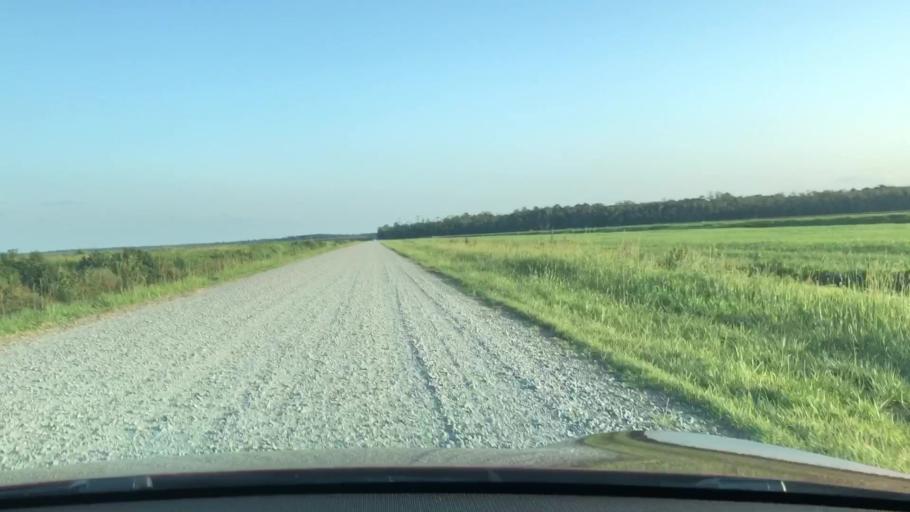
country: US
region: North Carolina
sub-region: Dare County
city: Manteo
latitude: 35.8527
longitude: -75.8620
